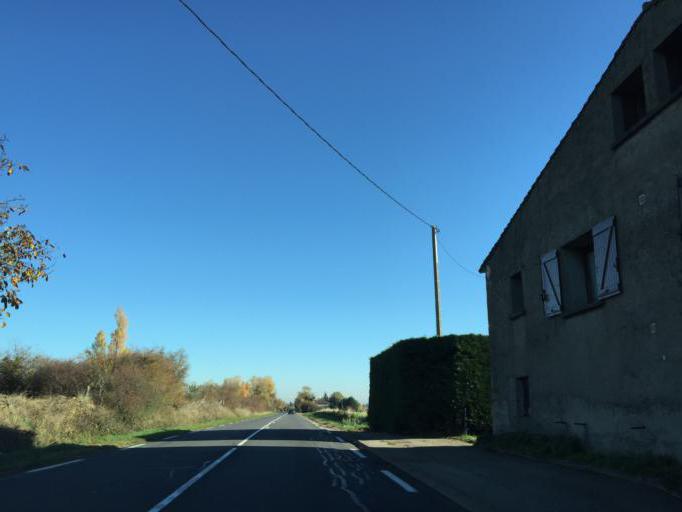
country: FR
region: Rhone-Alpes
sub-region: Departement du Rhone
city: Saint-Maurice-sur-Dargoire
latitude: 45.5702
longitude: 4.6452
